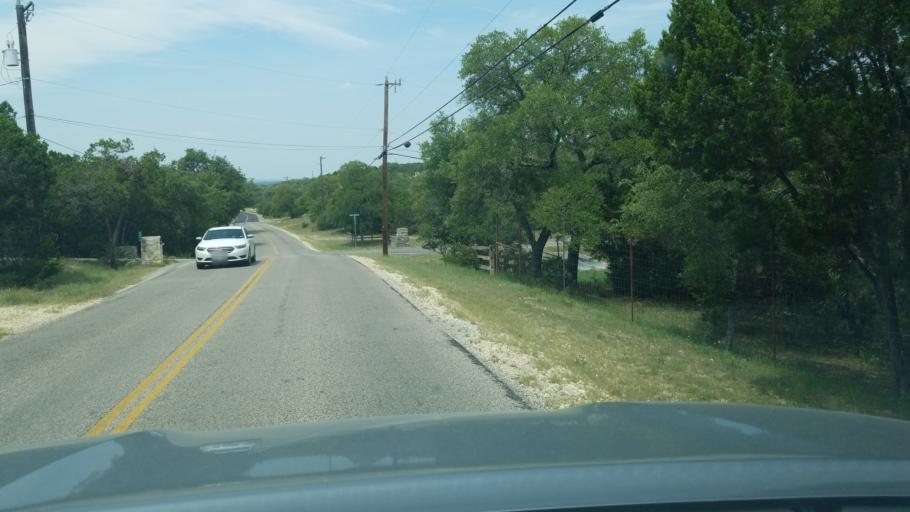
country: US
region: Texas
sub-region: Comal County
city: Bulverde
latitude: 29.7756
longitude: -98.4412
